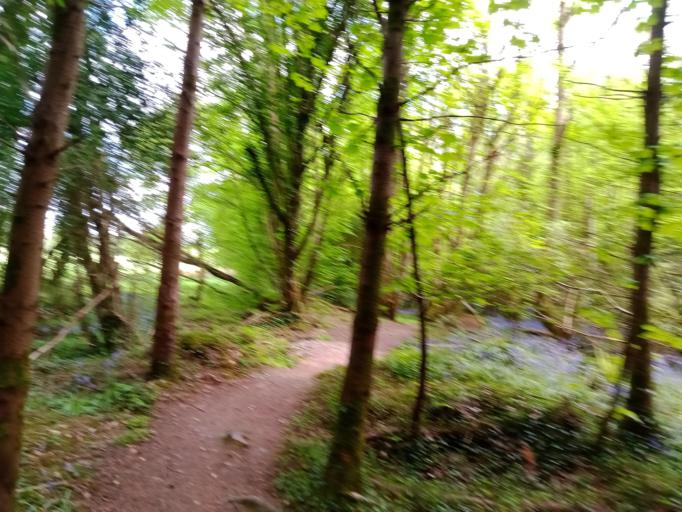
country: IE
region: Leinster
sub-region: Kilkenny
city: Castlecomer
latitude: 52.8215
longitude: -7.2055
